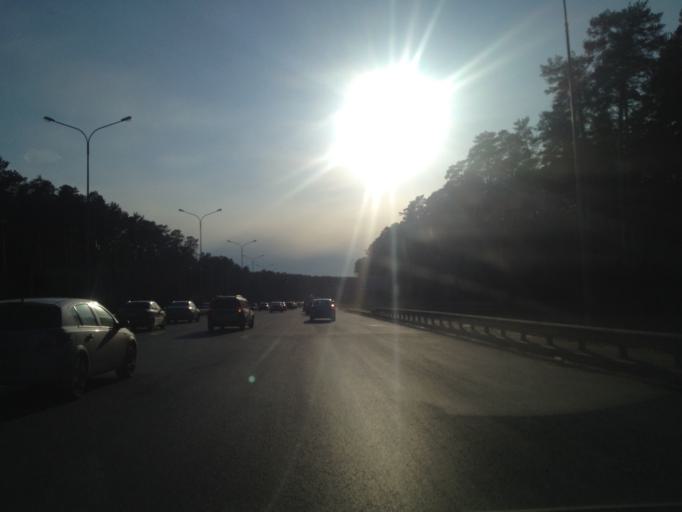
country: RU
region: Sverdlovsk
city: Sovkhoznyy
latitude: 56.7895
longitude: 60.5928
